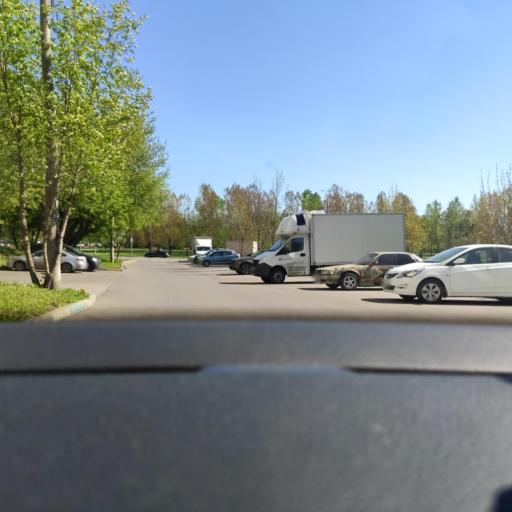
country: RU
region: Moscow
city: Kozeyevo
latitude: 55.8706
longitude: 37.6271
